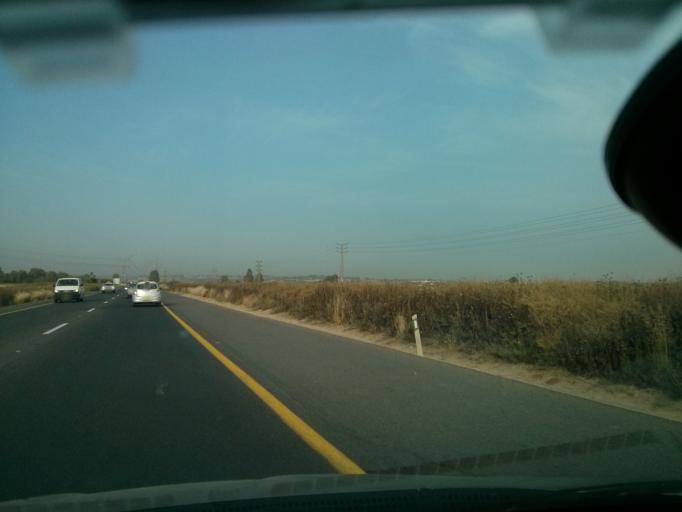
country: IL
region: Central District
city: Bene 'Ayish
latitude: 31.7091
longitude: 34.7285
